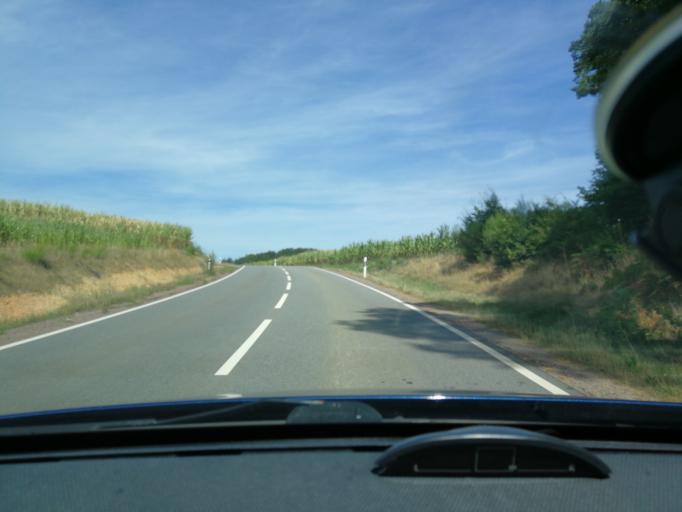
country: DE
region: Rheinland-Pfalz
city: Niersbach
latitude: 49.9272
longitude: 6.7558
